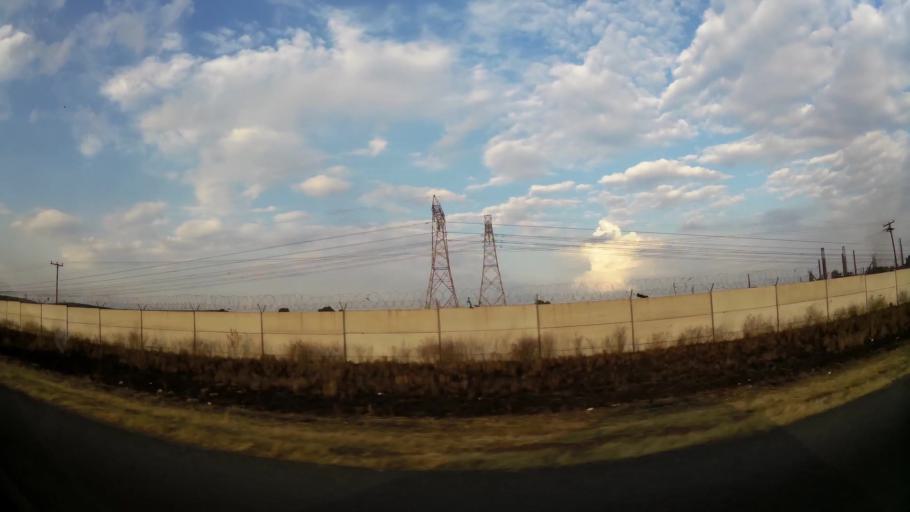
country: ZA
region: Gauteng
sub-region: Sedibeng District Municipality
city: Vanderbijlpark
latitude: -26.6480
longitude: 27.8037
